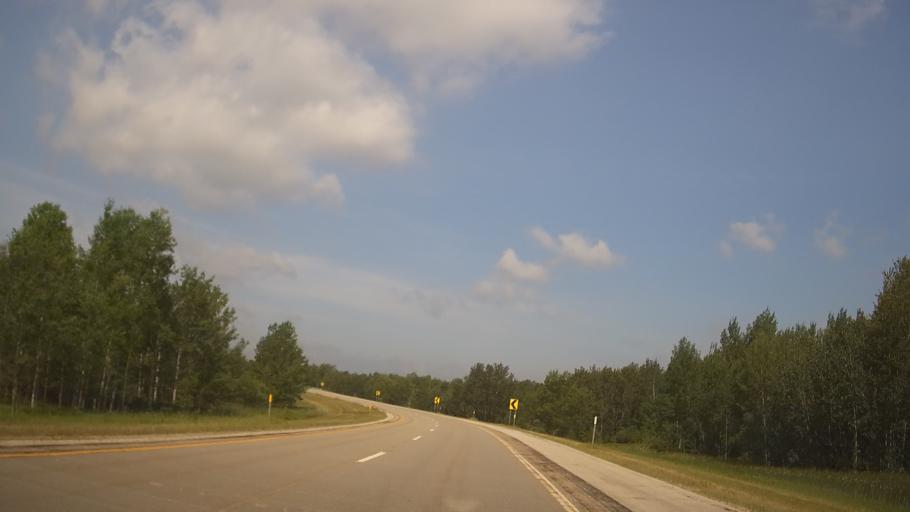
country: US
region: Michigan
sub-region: Roscommon County
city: Saint Helen
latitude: 44.3151
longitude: -84.4951
